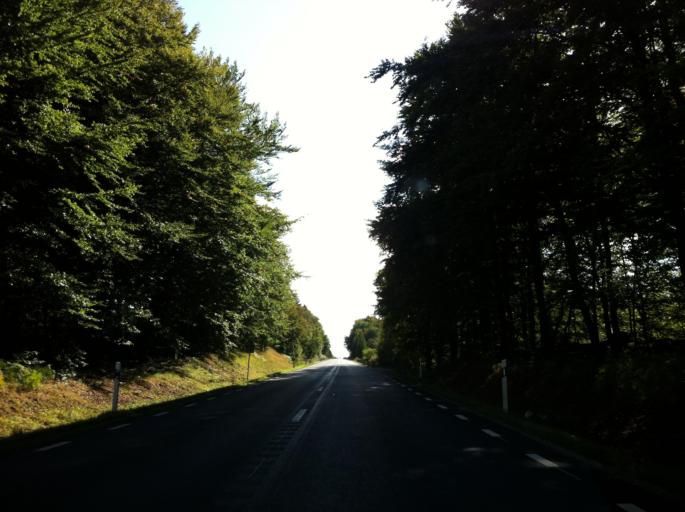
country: SE
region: Skane
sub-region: Tomelilla Kommun
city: Tomelilla
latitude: 55.6701
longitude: 14.0318
